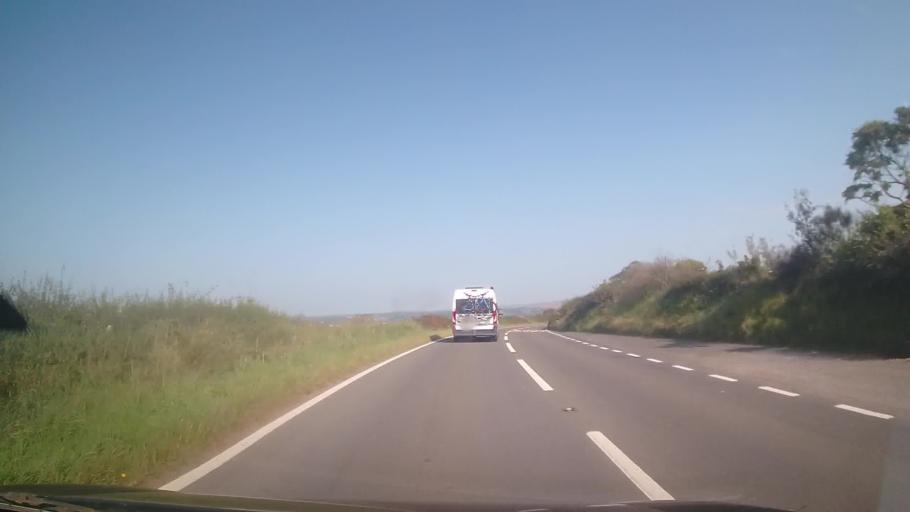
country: GB
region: Wales
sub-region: County of Ceredigion
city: Cardigan
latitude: 52.0680
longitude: -4.6784
